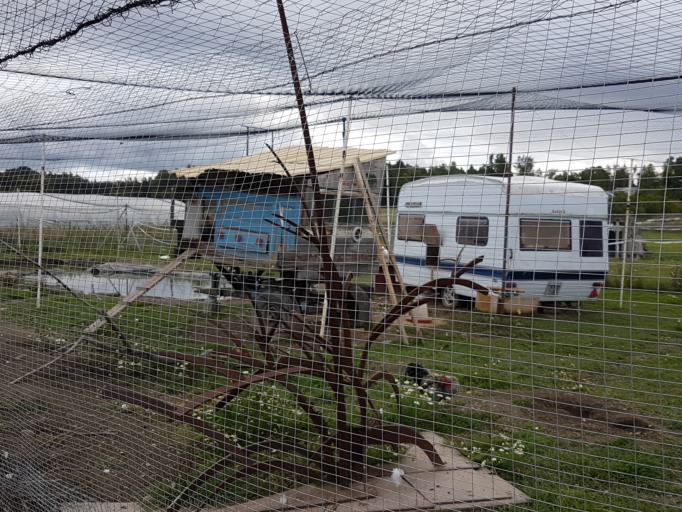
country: SE
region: Stockholm
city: Stenhamra
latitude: 59.2942
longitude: 17.7165
